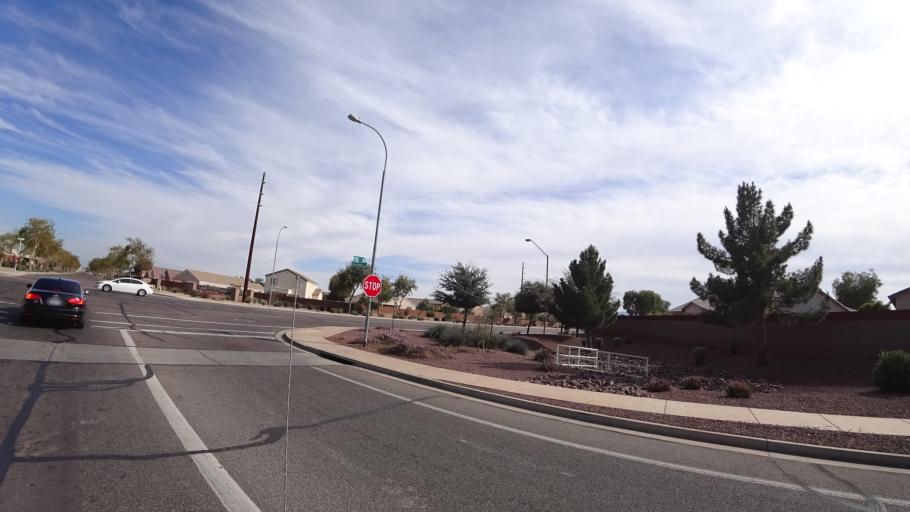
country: US
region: Arizona
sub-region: Maricopa County
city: Tolleson
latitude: 33.4281
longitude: -112.2901
